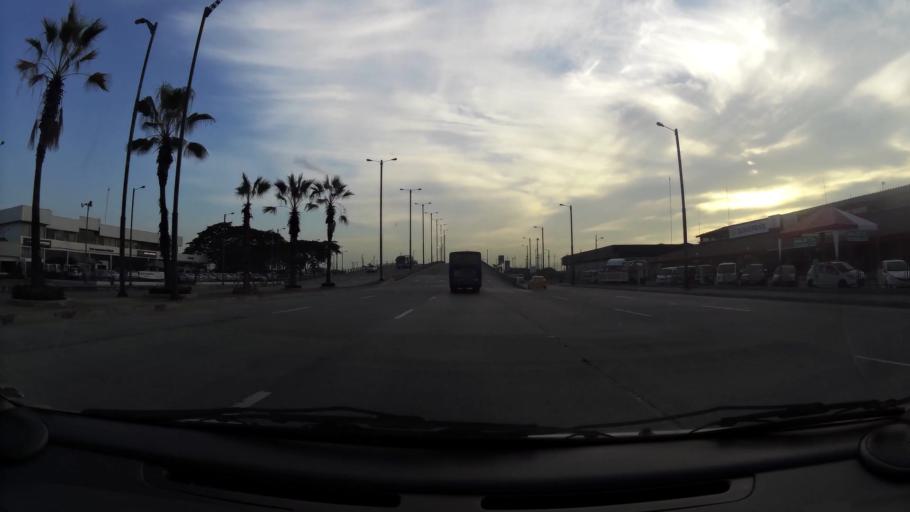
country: EC
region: Guayas
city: Eloy Alfaro
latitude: -2.1421
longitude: -79.8833
